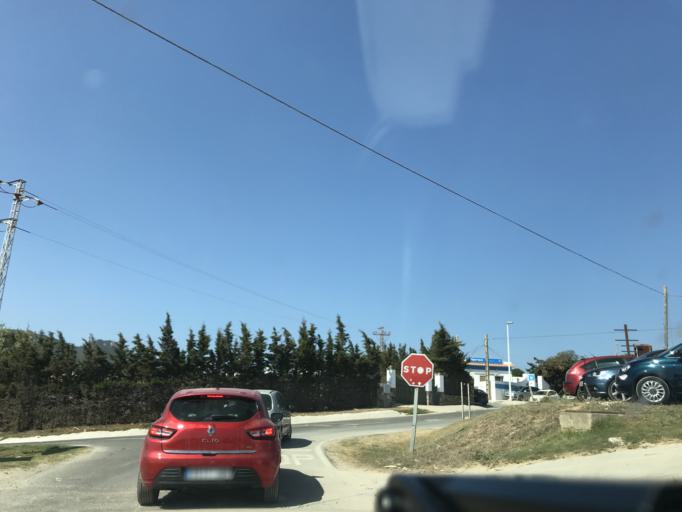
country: ES
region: Andalusia
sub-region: Provincia de Cadiz
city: Zahara de los Atunes
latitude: 36.0875
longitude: -5.7678
